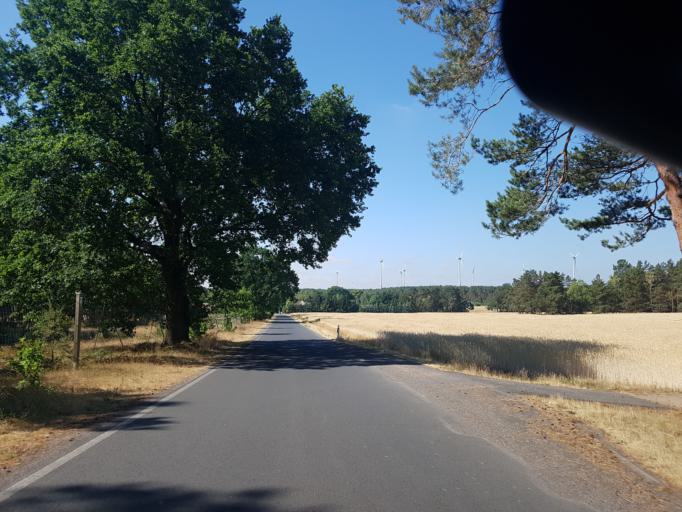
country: DE
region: Brandenburg
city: Treuenbrietzen
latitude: 52.0435
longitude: 12.8686
